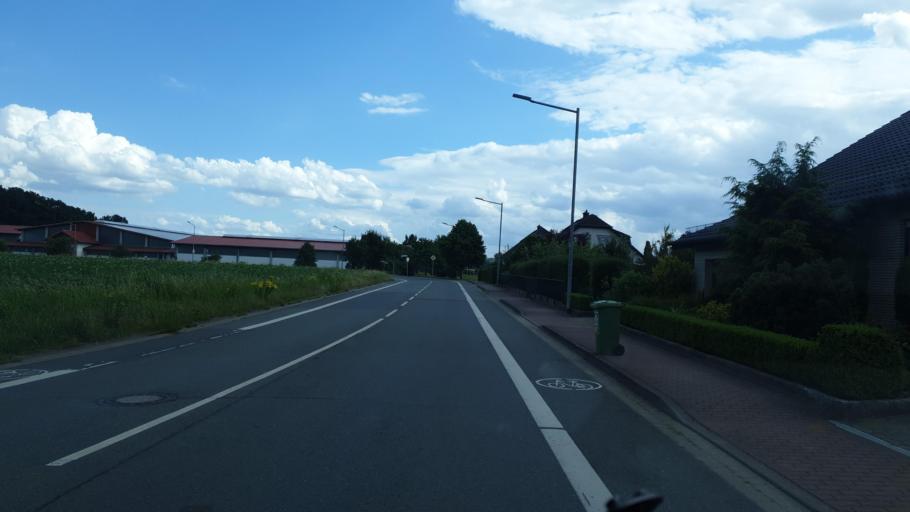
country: DE
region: North Rhine-Westphalia
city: Loehne
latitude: 52.2112
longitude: 8.7424
